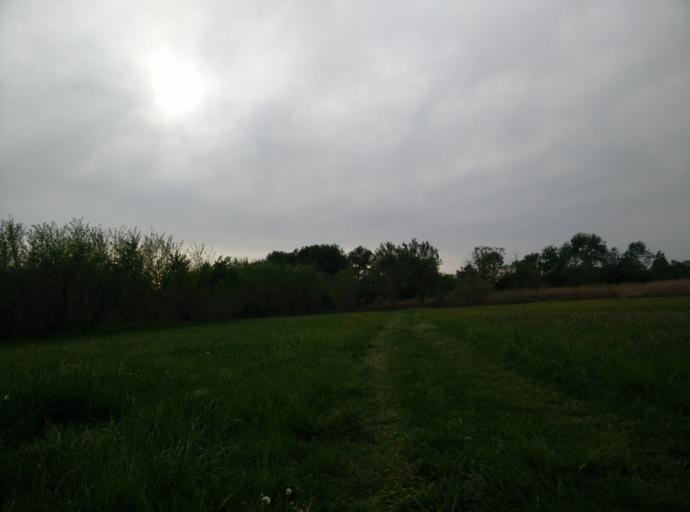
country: HU
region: Pest
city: Fot
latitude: 47.6073
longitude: 19.1779
